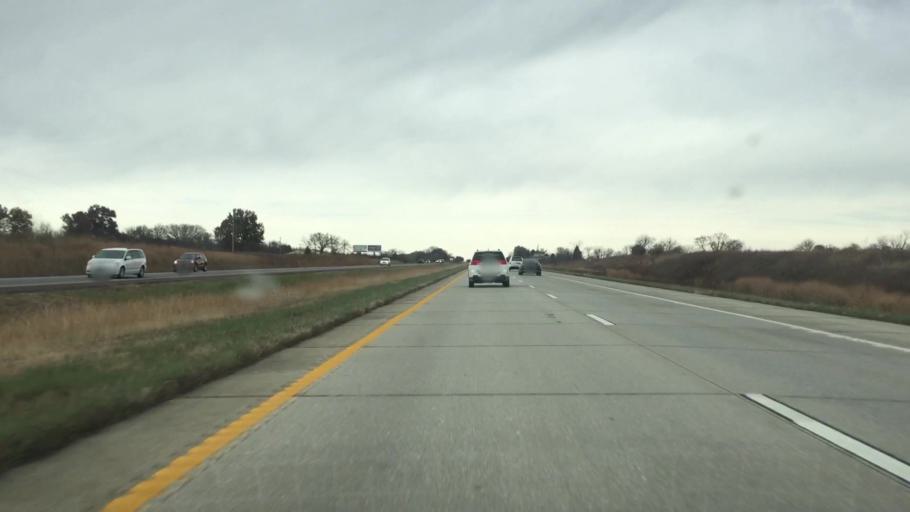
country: US
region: Missouri
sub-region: Saint Clair County
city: Osceola
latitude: 38.0896
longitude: -93.7074
